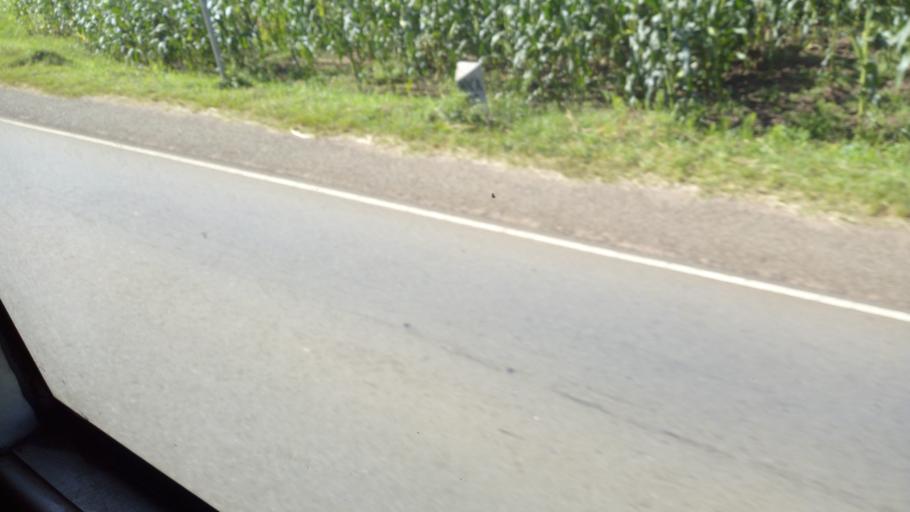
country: UG
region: Central Region
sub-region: Lyantonde District
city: Lyantonde
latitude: -0.3836
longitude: 31.2263
